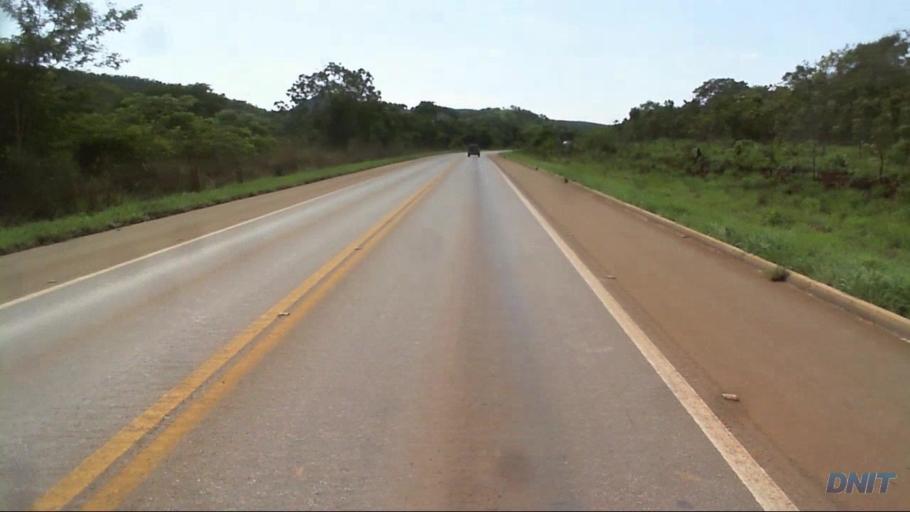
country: BR
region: Goias
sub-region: Barro Alto
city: Barro Alto
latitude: -15.1557
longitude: -48.8039
